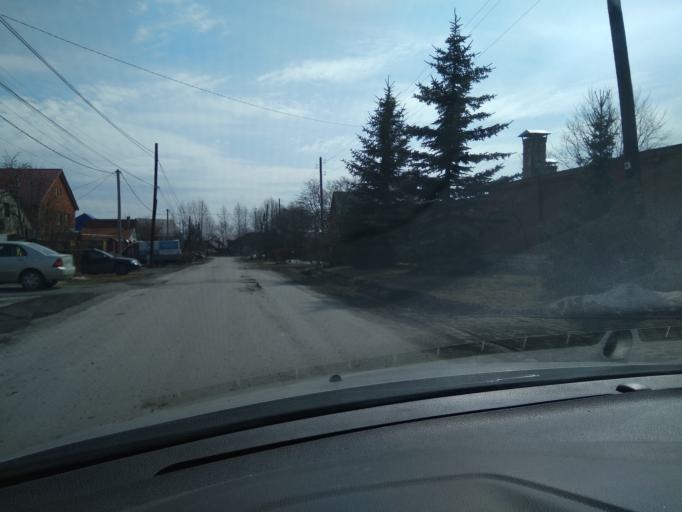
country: RU
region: Sverdlovsk
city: Shuvakish
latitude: 56.8885
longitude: 60.4856
